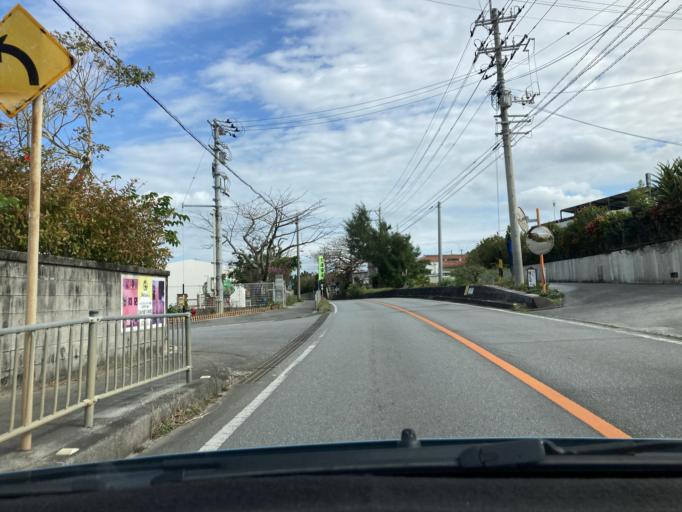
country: JP
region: Okinawa
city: Nago
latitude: 26.6971
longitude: 127.9353
